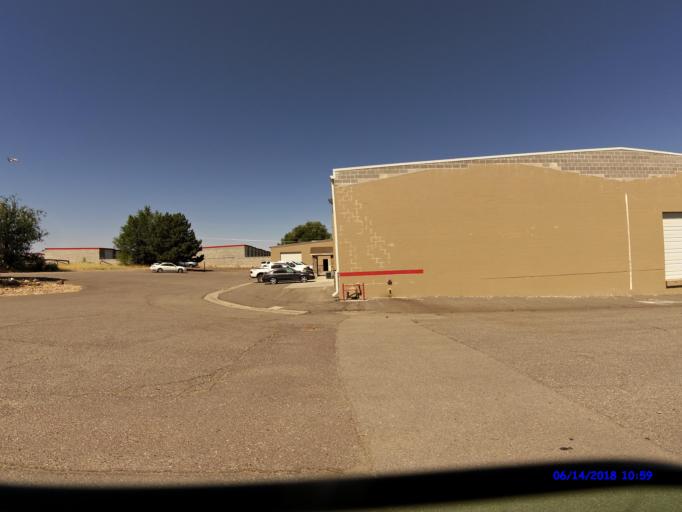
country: US
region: Utah
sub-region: Weber County
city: Riverdale
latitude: 41.2045
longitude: -112.0120
